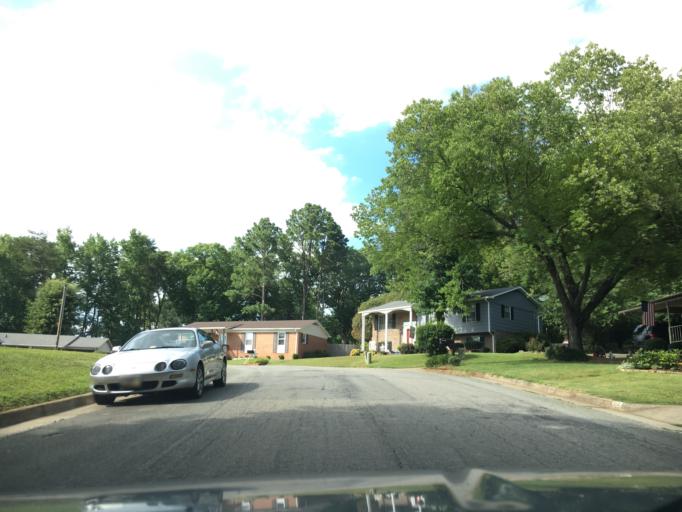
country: US
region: Virginia
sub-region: Halifax County
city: South Boston
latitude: 36.7133
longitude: -78.9067
